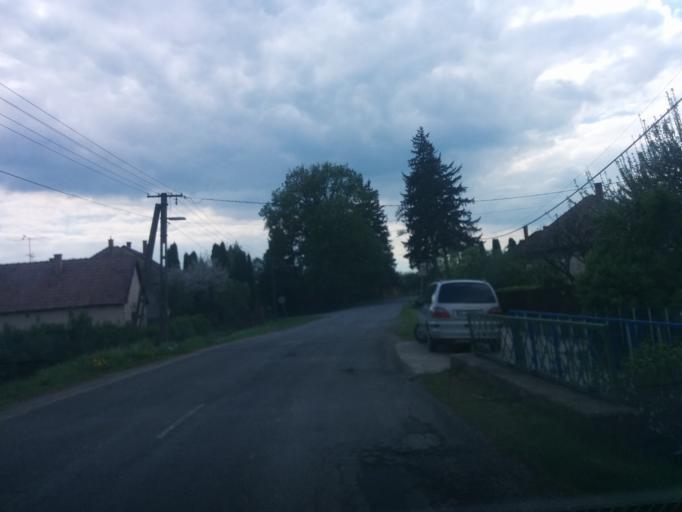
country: HU
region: Nograd
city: Romhany
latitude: 47.8430
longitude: 19.3015
